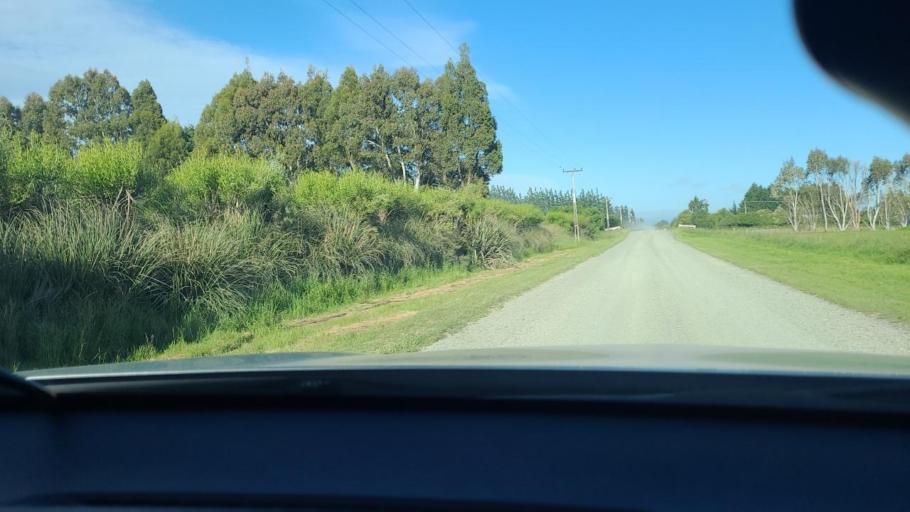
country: NZ
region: Southland
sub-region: Southland District
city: Winton
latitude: -46.0067
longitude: 168.1603
